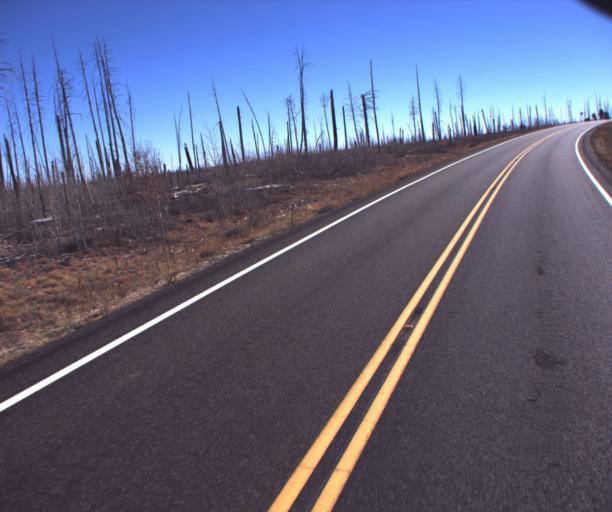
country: US
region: Arizona
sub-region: Coconino County
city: Fredonia
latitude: 36.5866
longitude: -112.1772
